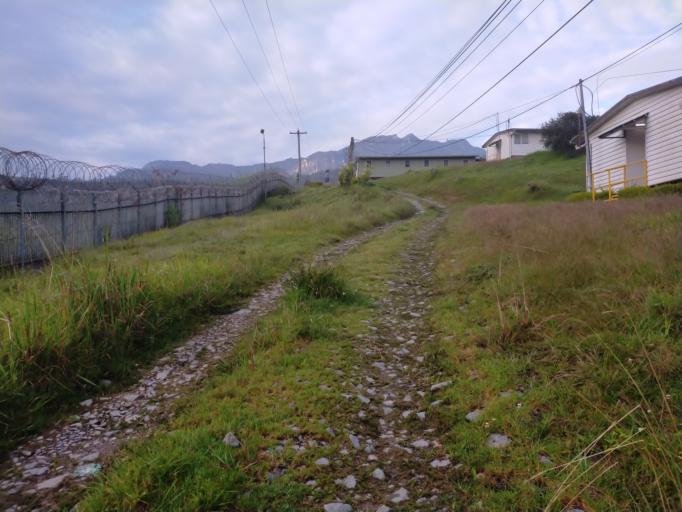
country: PG
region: Enga
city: Porgera
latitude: -5.4607
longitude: 143.1057
